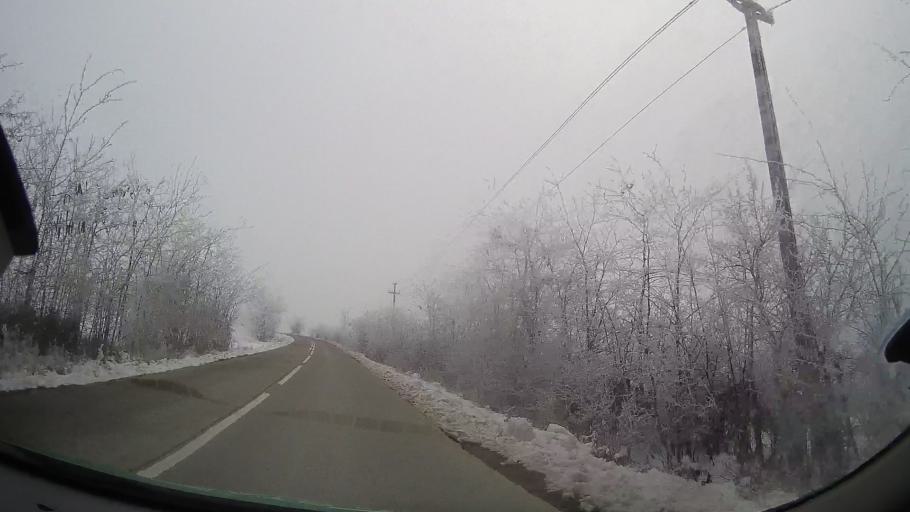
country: RO
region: Bacau
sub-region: Comuna Podu Turcului
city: Podu Turcului
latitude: 46.2094
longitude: 27.4177
